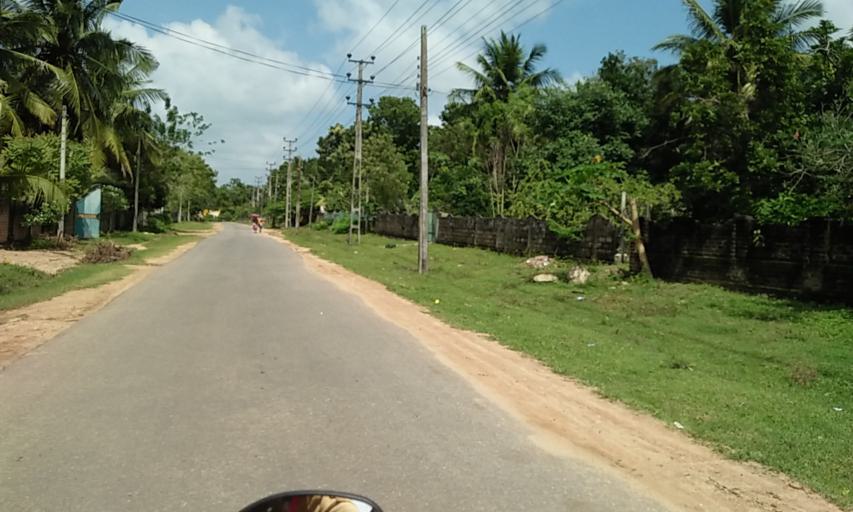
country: LK
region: Eastern Province
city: Ampara
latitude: 7.3344
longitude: 81.7428
